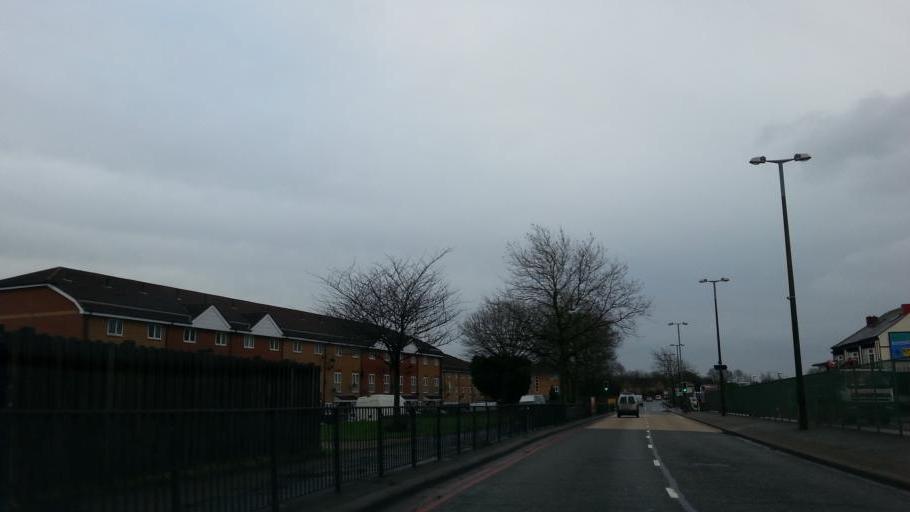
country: GB
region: England
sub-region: Sandwell
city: Smethwick
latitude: 52.5025
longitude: -1.9866
